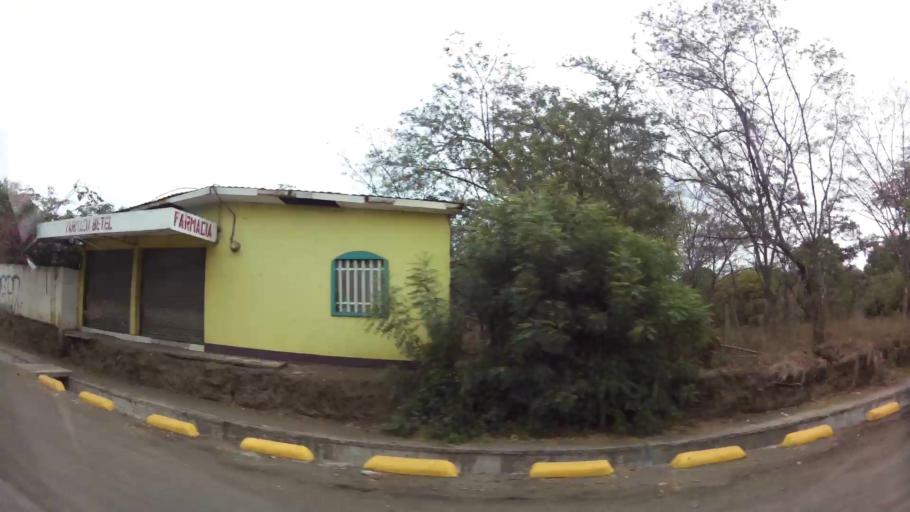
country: NI
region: Managua
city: Managua
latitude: 12.1230
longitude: -86.1715
